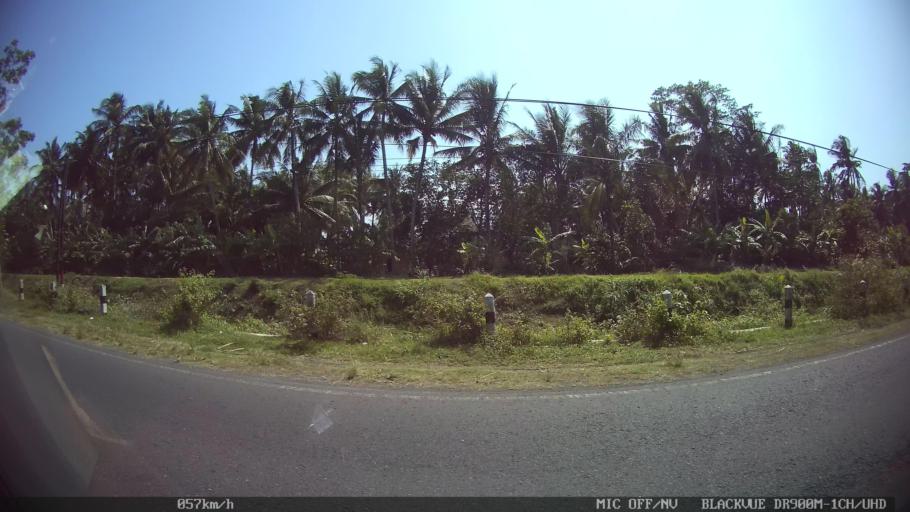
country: ID
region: Daerah Istimewa Yogyakarta
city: Srandakan
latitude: -7.9379
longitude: 110.1564
